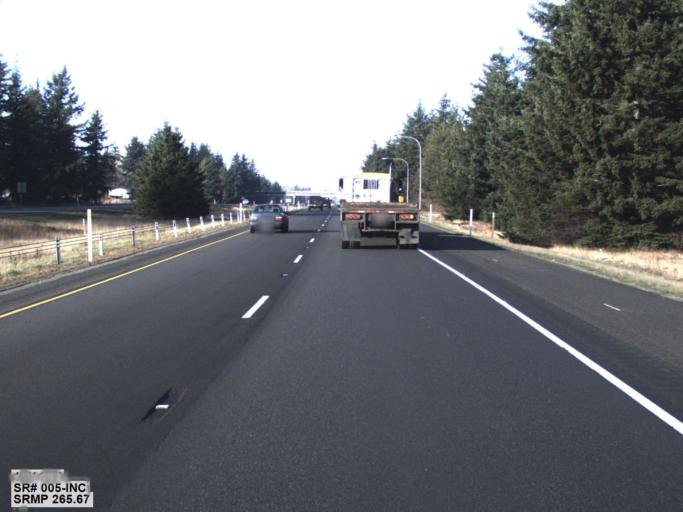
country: US
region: Washington
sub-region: Whatcom County
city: Ferndale
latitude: 48.8889
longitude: -122.5916
